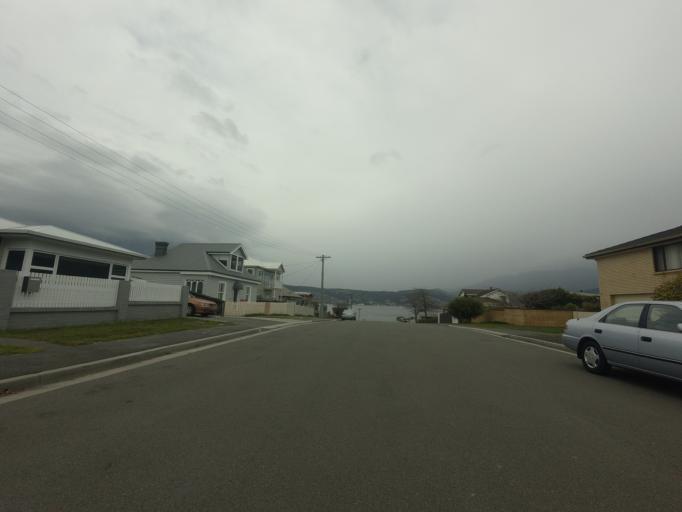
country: AU
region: Tasmania
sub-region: Clarence
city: Bellerive
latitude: -42.8781
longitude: 147.3669
